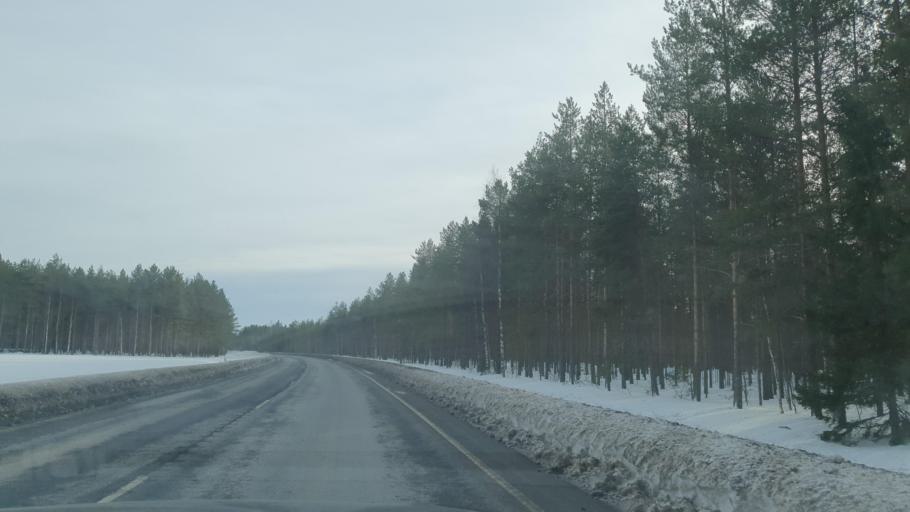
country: FI
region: Northern Ostrobothnia
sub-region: Oulunkaari
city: Utajaervi
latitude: 64.7066
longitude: 26.5184
